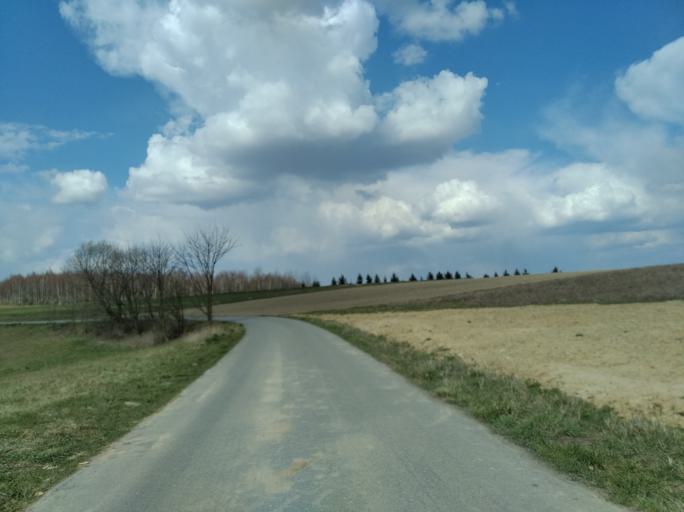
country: PL
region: Subcarpathian Voivodeship
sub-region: Powiat strzyzowski
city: Strzyzow
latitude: 49.9312
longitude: 21.7252
